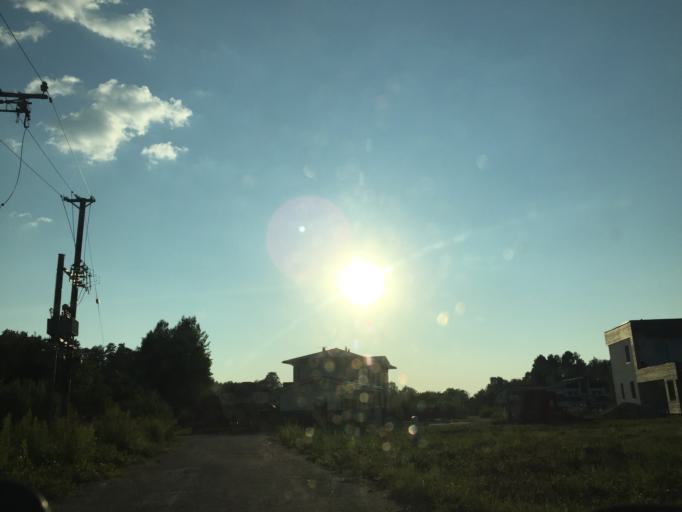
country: LV
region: Garkalne
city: Garkalne
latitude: 56.9798
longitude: 24.3824
